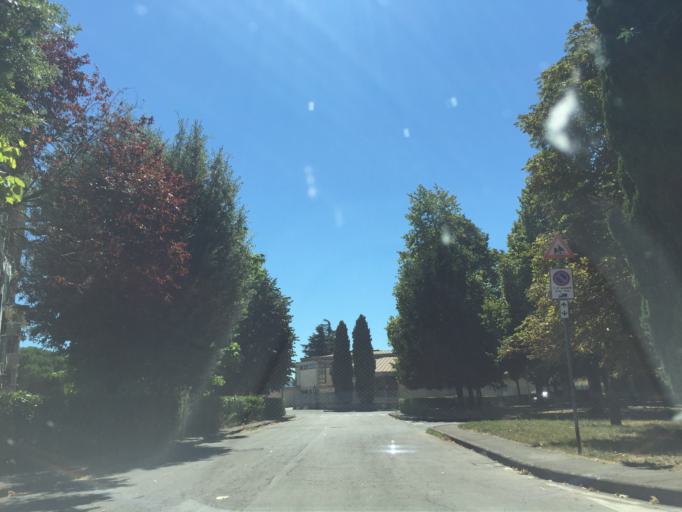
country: IT
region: Tuscany
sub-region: Provincia di Pistoia
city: Pistoia
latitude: 43.9501
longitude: 10.9023
